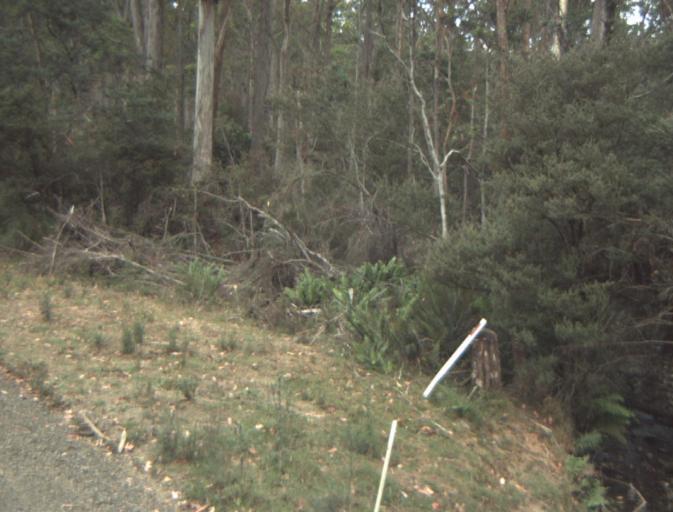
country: AU
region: Tasmania
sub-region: Dorset
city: Scottsdale
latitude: -41.4090
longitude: 147.5175
